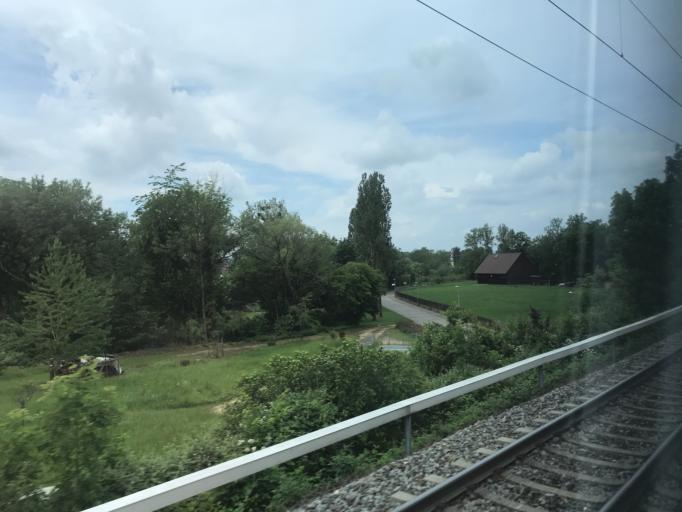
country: DE
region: Baden-Wuerttemberg
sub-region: Regierungsbezirk Stuttgart
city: Sussen
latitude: 48.6775
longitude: 9.7692
